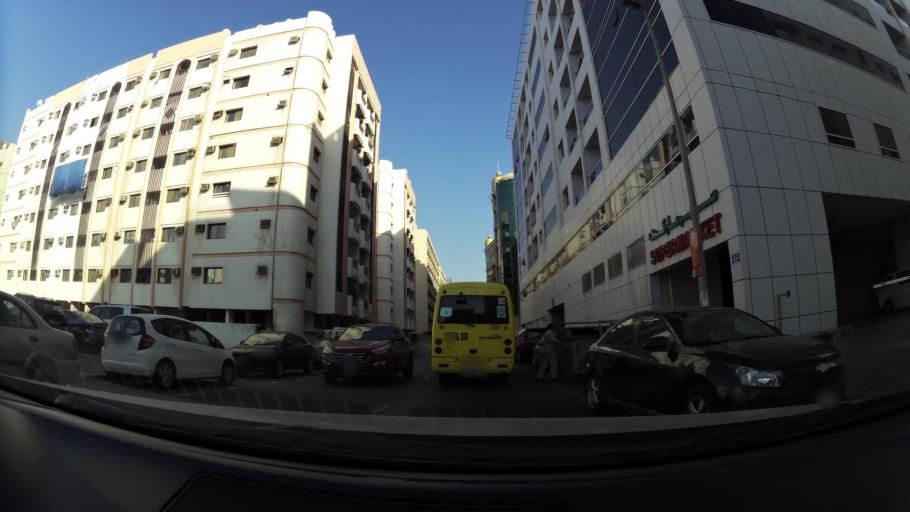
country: AE
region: Ash Shariqah
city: Sharjah
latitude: 25.2649
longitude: 55.3254
